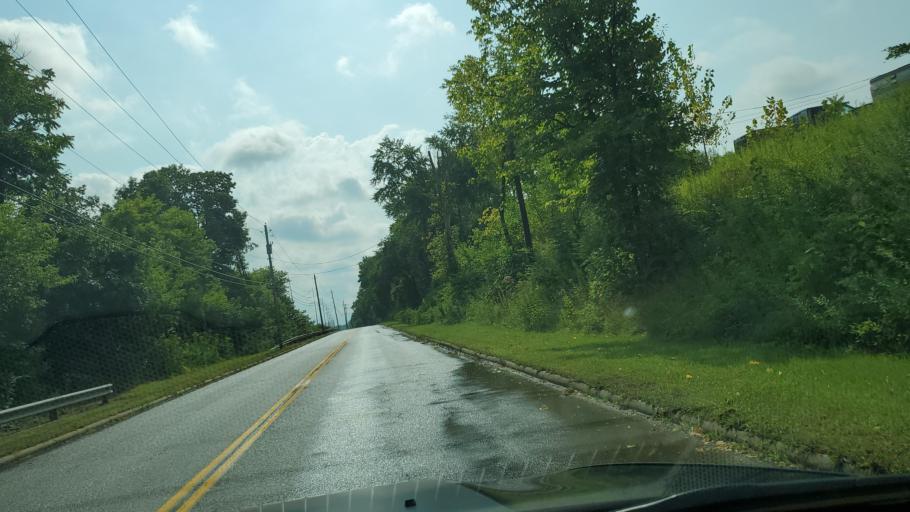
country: US
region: Ohio
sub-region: Mahoning County
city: Struthers
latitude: 41.0498
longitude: -80.5775
